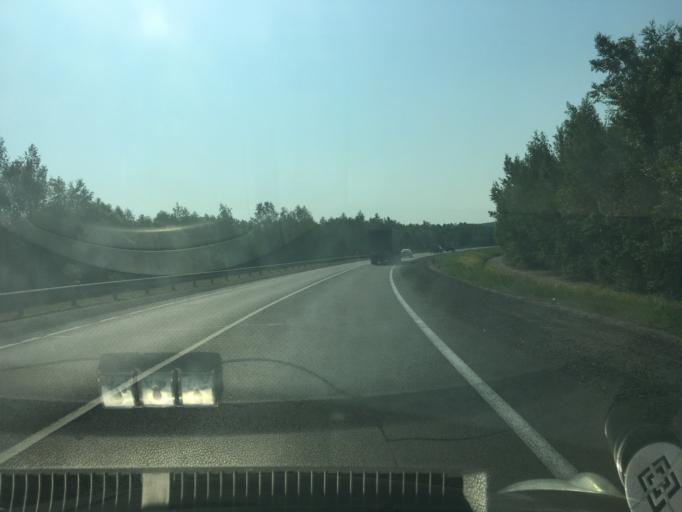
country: RU
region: Nizjnij Novgorod
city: Pamyat' Parizhskoy Kommuny
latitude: 56.0781
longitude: 44.3682
